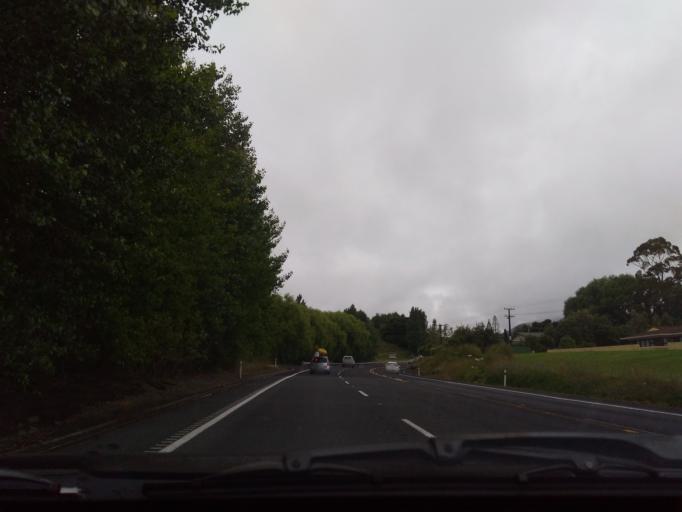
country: NZ
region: Auckland
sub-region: Auckland
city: Wellsford
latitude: -36.1539
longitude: 174.4394
